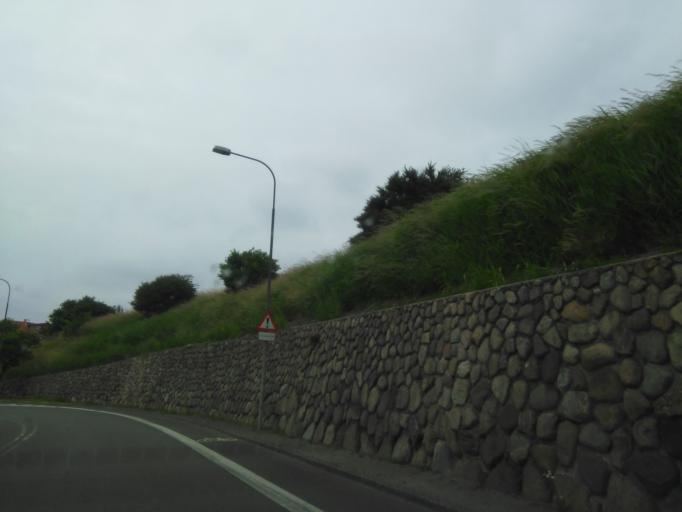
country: DK
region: Capital Region
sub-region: Bornholm Kommune
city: Ronne
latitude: 55.0956
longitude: 14.6991
